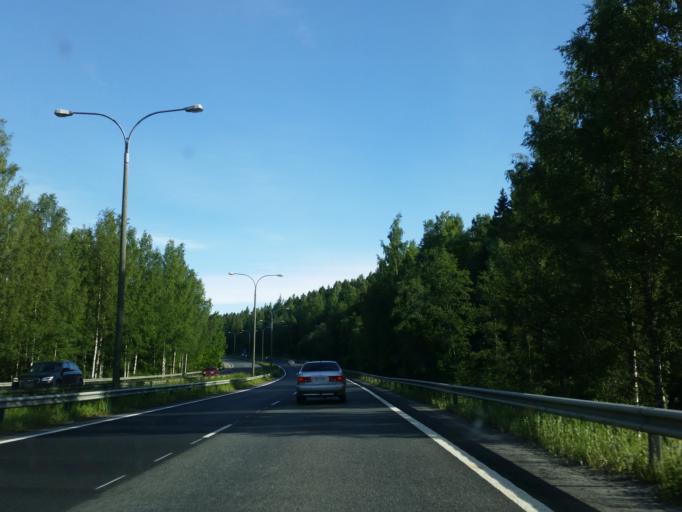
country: FI
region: Northern Savo
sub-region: Kuopio
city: Kuopio
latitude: 62.9181
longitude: 27.6781
